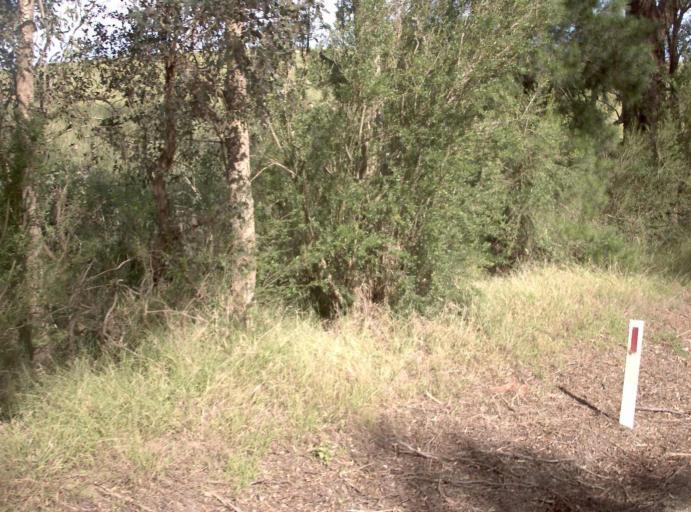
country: AU
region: Victoria
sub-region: East Gippsland
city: Lakes Entrance
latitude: -37.5192
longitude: 148.1620
